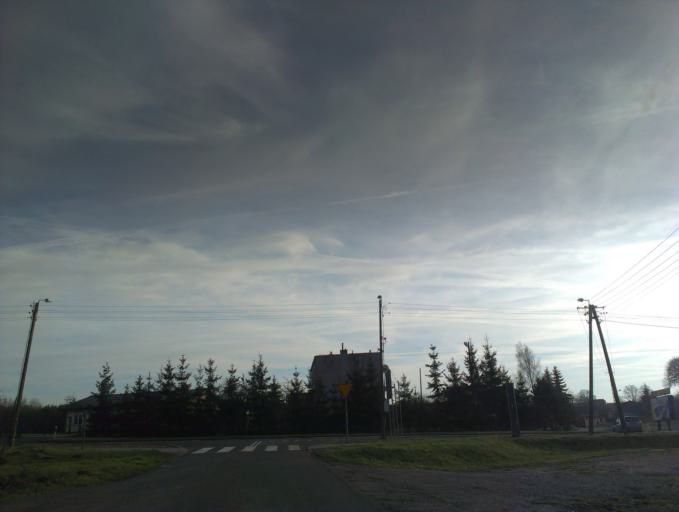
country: PL
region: Pomeranian Voivodeship
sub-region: Powiat czluchowski
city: Debrzno
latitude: 53.6144
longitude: 17.1878
